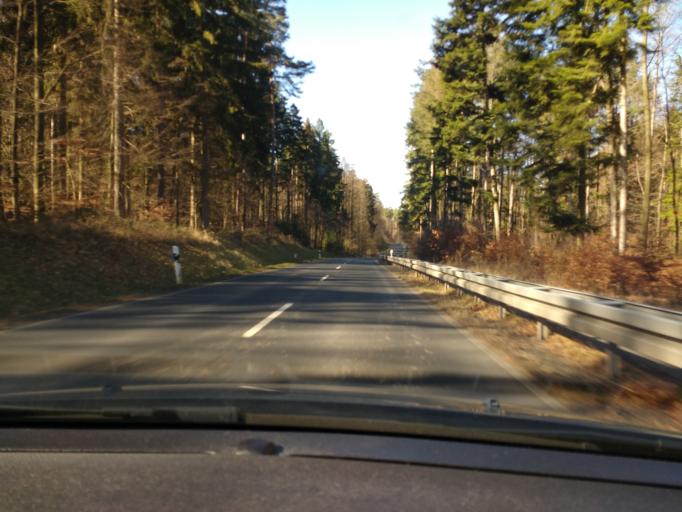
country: DE
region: Bavaria
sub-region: Regierungsbezirk Unterfranken
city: Alzenau in Unterfranken
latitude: 50.1280
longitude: 9.0788
